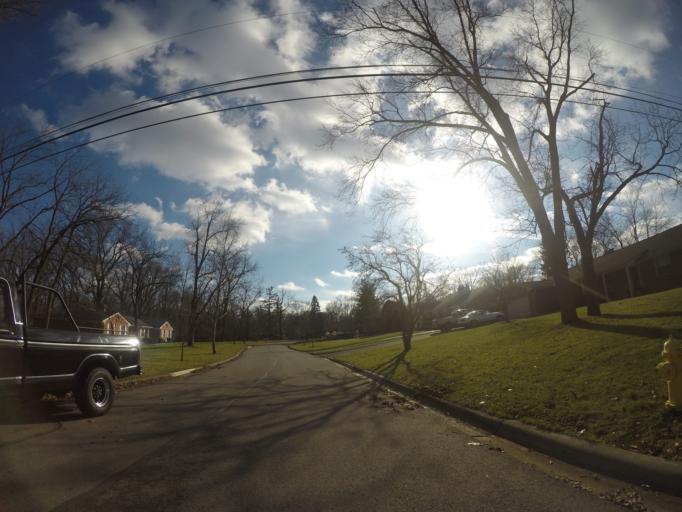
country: US
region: Ohio
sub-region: Franklin County
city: Upper Arlington
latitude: 40.0332
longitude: -83.0798
